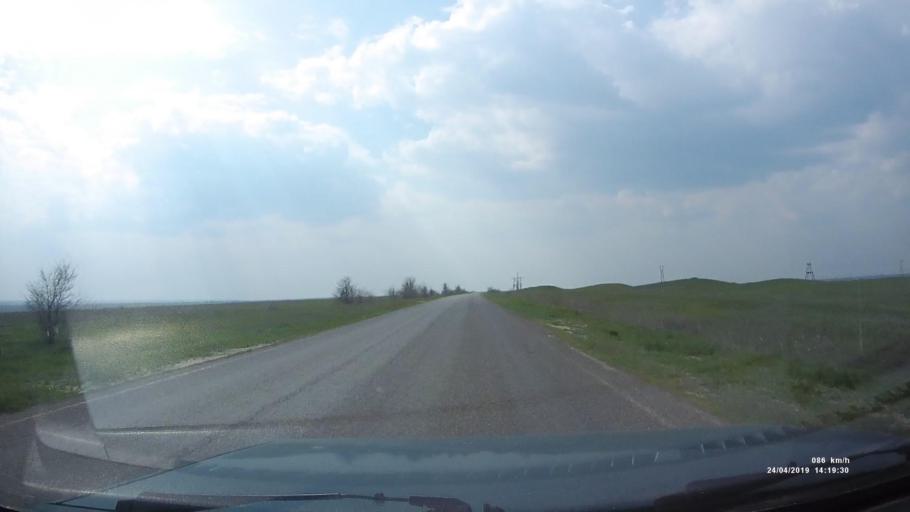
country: RU
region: Kalmykiya
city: Arshan'
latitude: 46.3056
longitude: 44.1747
